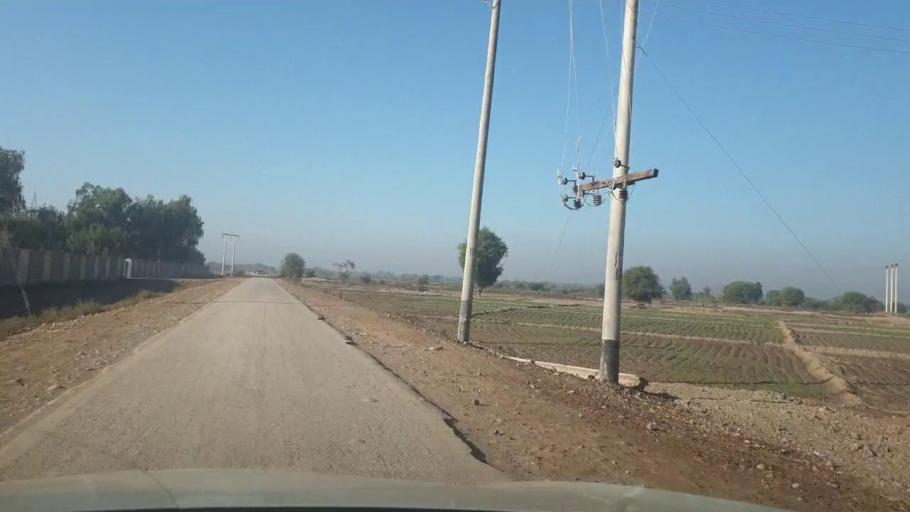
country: PK
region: Sindh
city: Bhan
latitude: 26.5502
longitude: 67.7139
